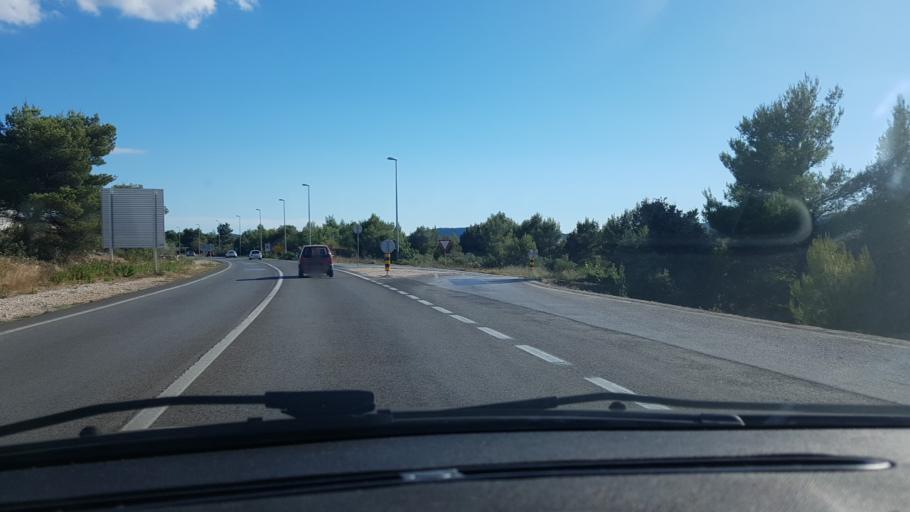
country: HR
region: Sibensko-Kniniska
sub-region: Grad Sibenik
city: Brodarica
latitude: 43.6977
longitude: 15.9041
